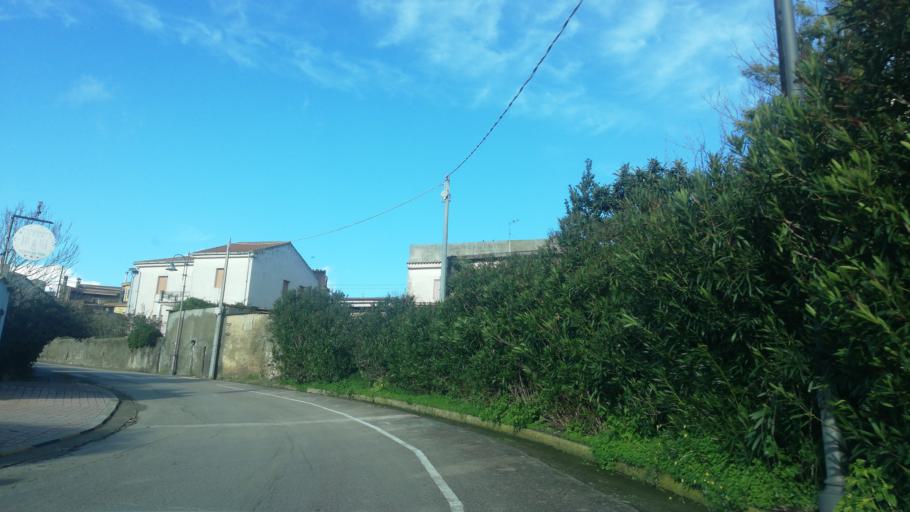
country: IT
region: Sardinia
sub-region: Provincia di Medio Campidano
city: Villanovaforru
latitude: 39.6308
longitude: 8.8729
